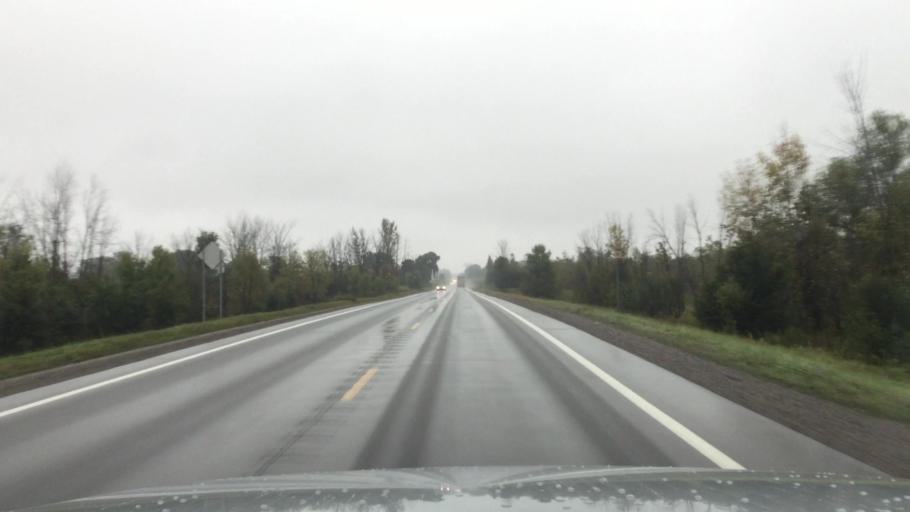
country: US
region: Michigan
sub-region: Saginaw County
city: Saginaw
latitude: 43.3630
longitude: -83.9548
